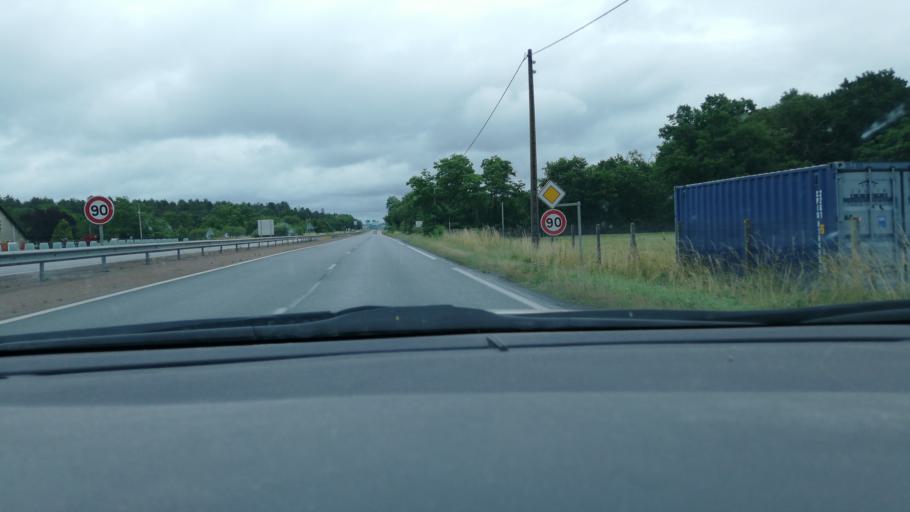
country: FR
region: Poitou-Charentes
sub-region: Departement de la Vienne
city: Naintre
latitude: 46.7729
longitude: 0.5104
